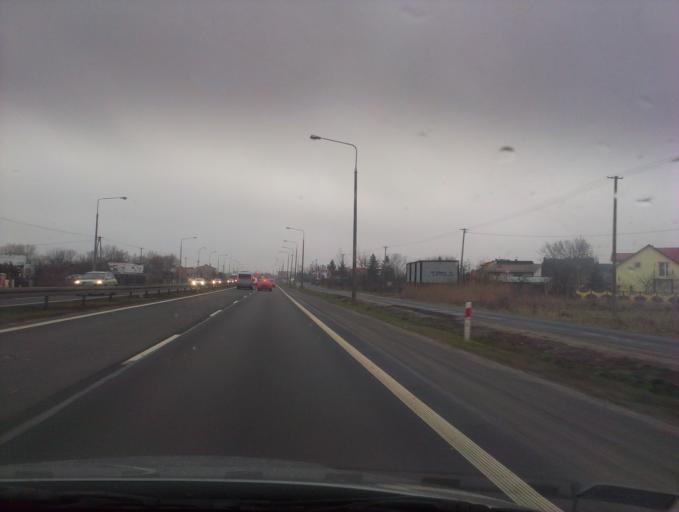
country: PL
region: Masovian Voivodeship
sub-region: Powiat radomski
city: Jedlinsk
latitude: 51.4640
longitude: 21.1389
